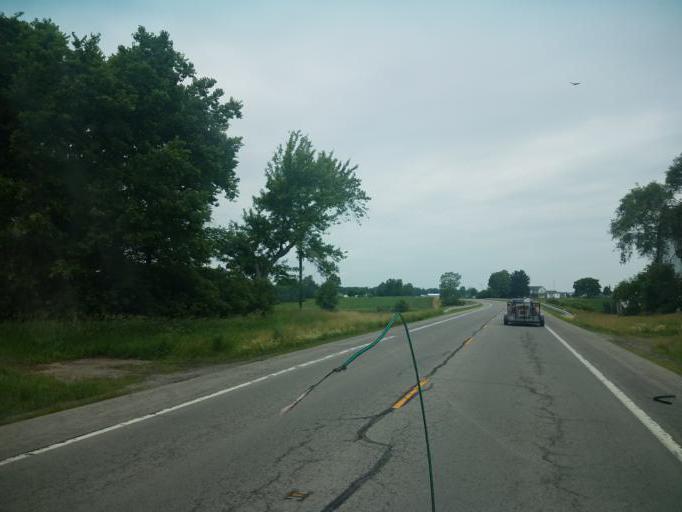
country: US
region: Ohio
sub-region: Hardin County
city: Ada
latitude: 40.7162
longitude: -83.7627
